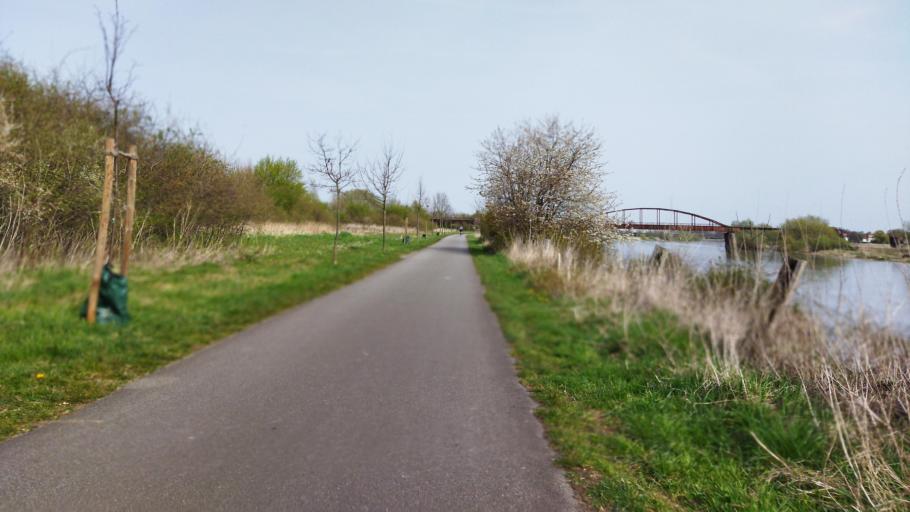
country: DE
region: North Rhine-Westphalia
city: Porta Westfalica
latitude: 52.2578
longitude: 8.9177
